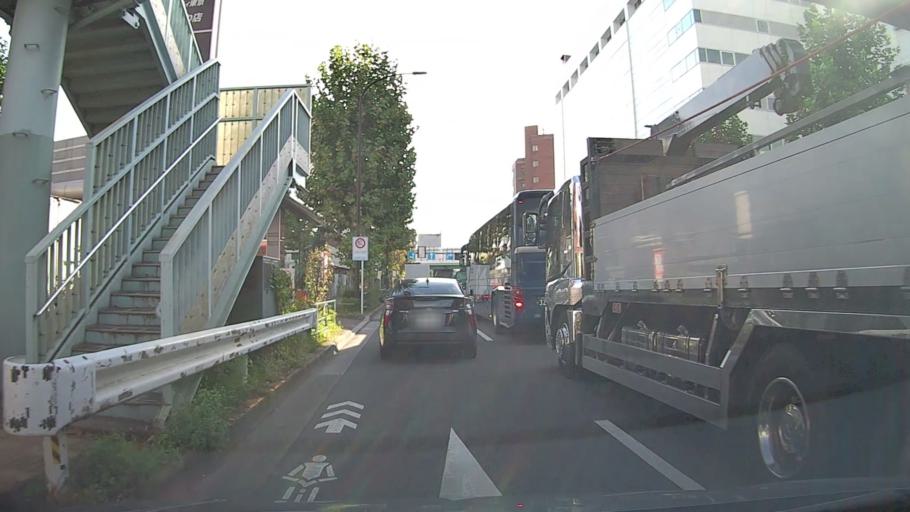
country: JP
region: Tokyo
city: Tokyo
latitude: 35.7351
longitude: 139.6606
